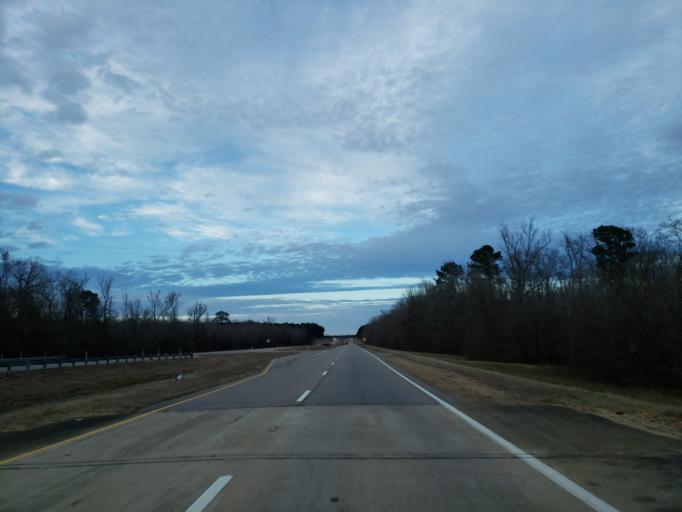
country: US
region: Mississippi
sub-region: Kemper County
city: De Kalb
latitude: 32.6999
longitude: -88.4845
